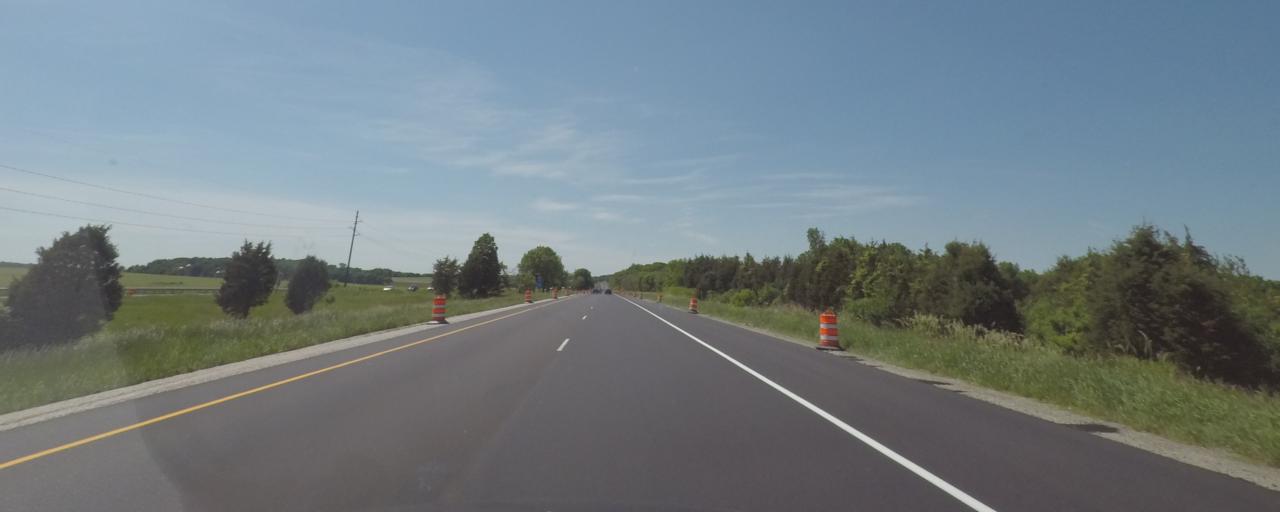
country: US
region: Wisconsin
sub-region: Jefferson County
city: Lake Mills
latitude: 43.1030
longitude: -88.9362
